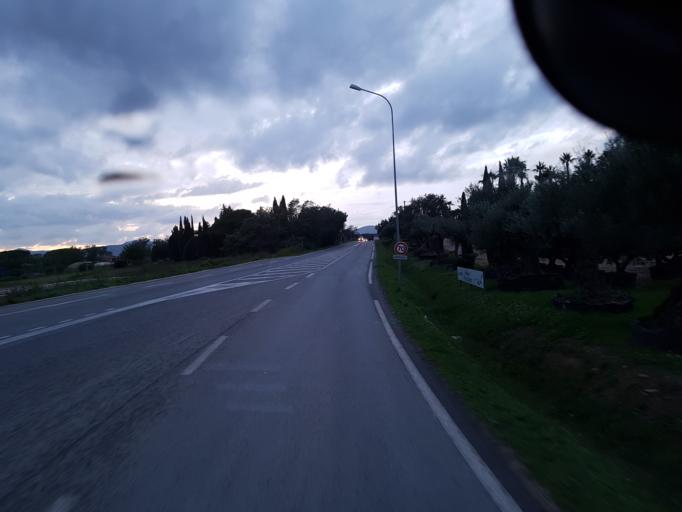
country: FR
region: Provence-Alpes-Cote d'Azur
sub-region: Departement du Var
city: Grimaud
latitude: 43.2700
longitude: 6.5411
